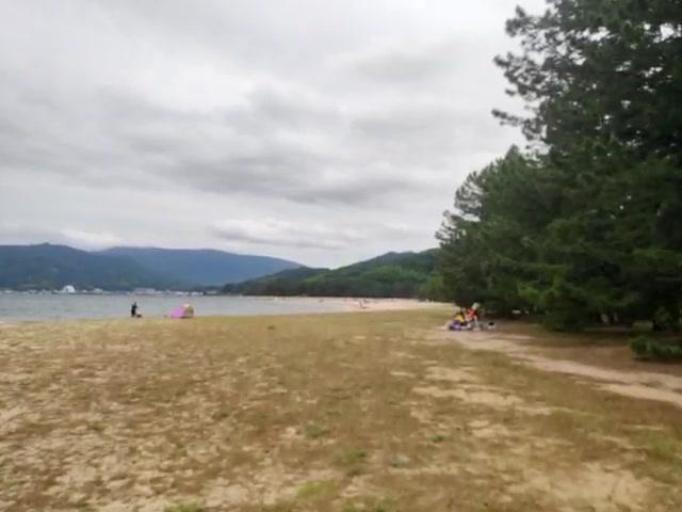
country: JP
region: Kyoto
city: Miyazu
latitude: 35.5610
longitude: 135.1878
